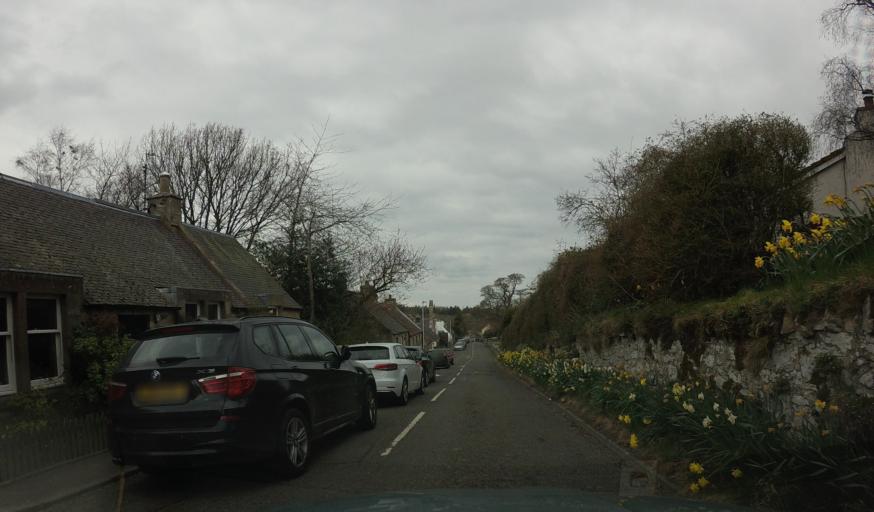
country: GB
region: Scotland
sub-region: Midlothian
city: Gorebridge
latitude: 55.8135
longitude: -3.0893
